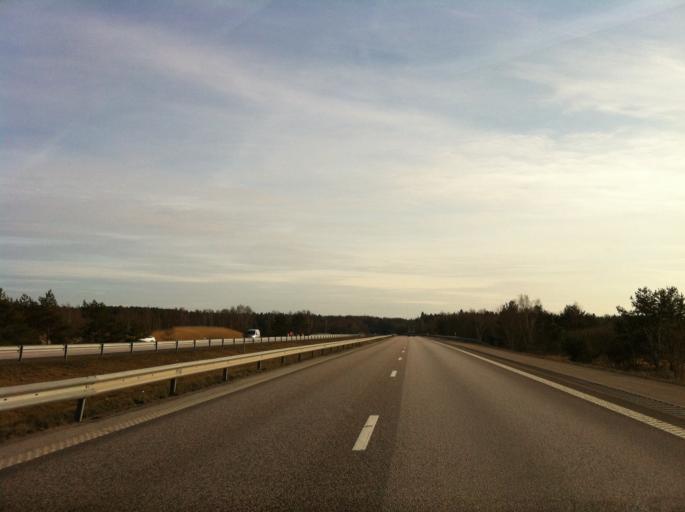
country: SE
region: Halland
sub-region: Kungsbacka Kommun
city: Fjaeras kyrkby
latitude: 57.4336
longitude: 12.1497
